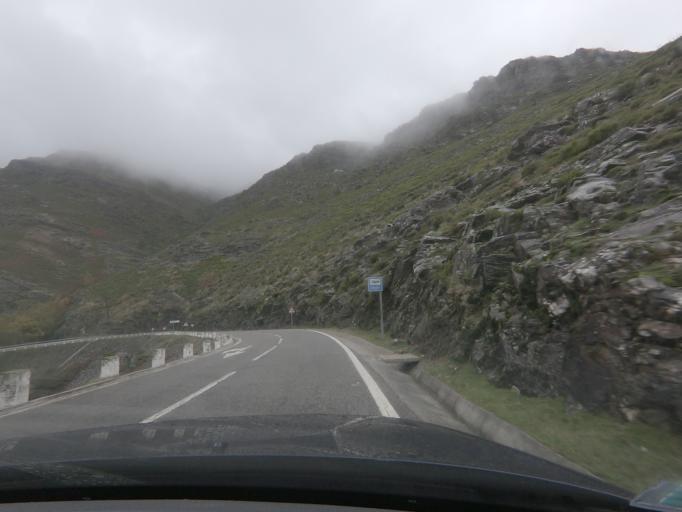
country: PT
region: Vila Real
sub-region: Mondim de Basto
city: Mondim de Basto
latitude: 41.3358
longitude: -7.8691
